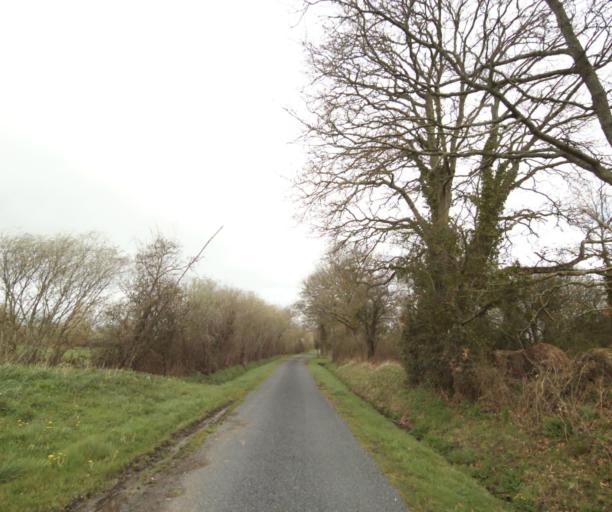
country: FR
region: Pays de la Loire
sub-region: Departement de la Loire-Atlantique
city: Bouvron
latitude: 47.4229
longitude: -1.8934
